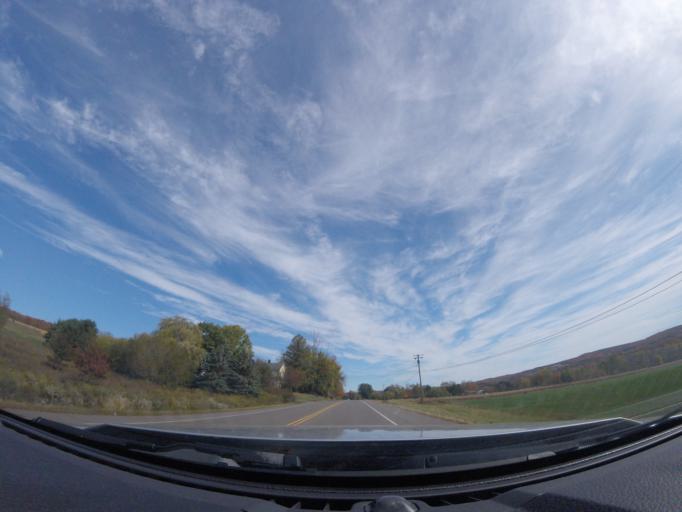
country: US
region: New York
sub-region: Cortland County
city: Cortland West
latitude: 42.5577
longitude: -76.2771
